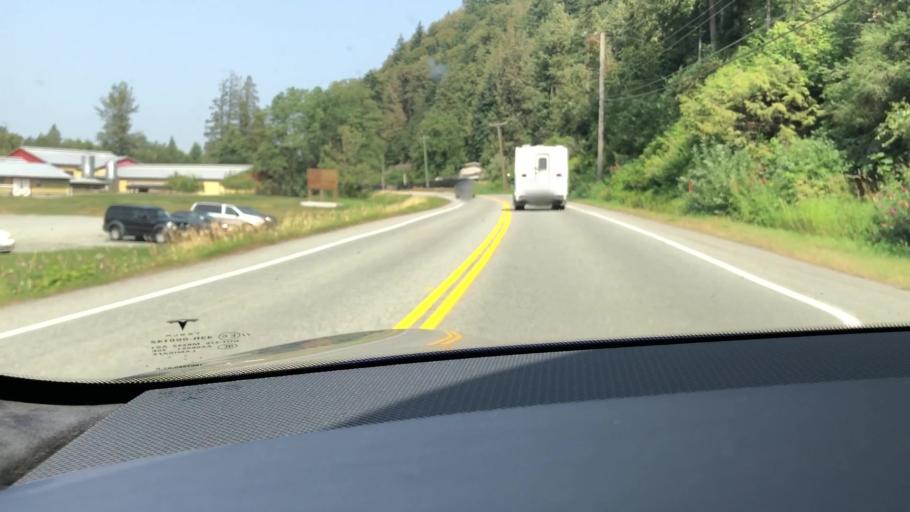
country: CA
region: British Columbia
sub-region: Fraser Valley Regional District
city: Chilliwack
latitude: 49.0833
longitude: -122.0309
